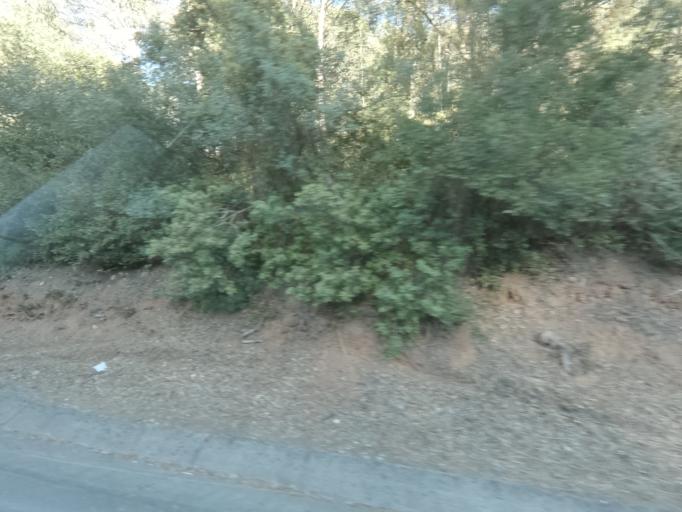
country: PT
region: Setubal
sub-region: Setubal
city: Setubal
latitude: 38.5094
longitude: -8.9251
